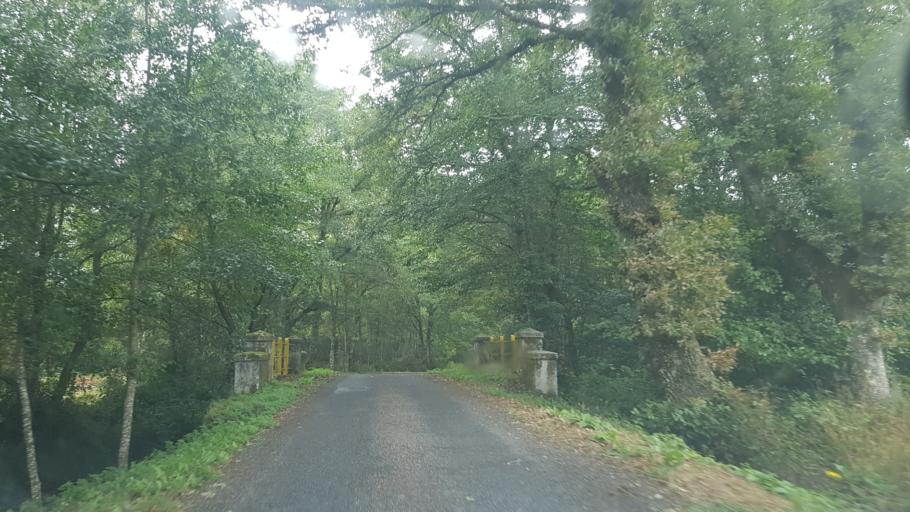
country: ES
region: Galicia
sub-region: Provincia de Lugo
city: Friol
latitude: 43.1226
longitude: -7.8159
